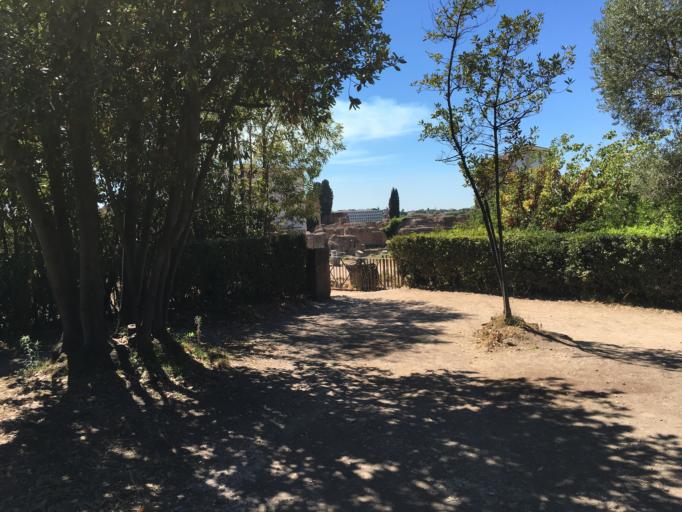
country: IT
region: Latium
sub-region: Citta metropolitana di Roma Capitale
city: Rome
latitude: 41.8896
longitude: 12.4860
